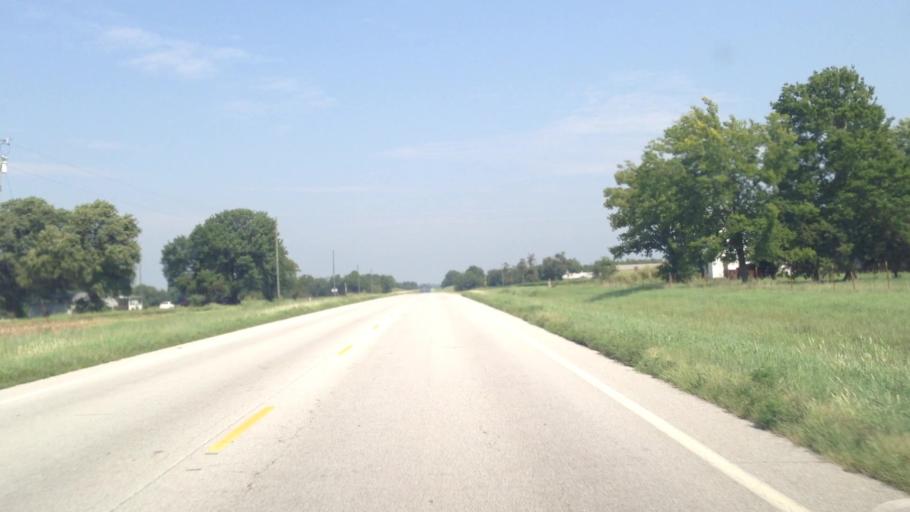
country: US
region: Kansas
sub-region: Labette County
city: Oswego
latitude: 37.1047
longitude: -95.1034
